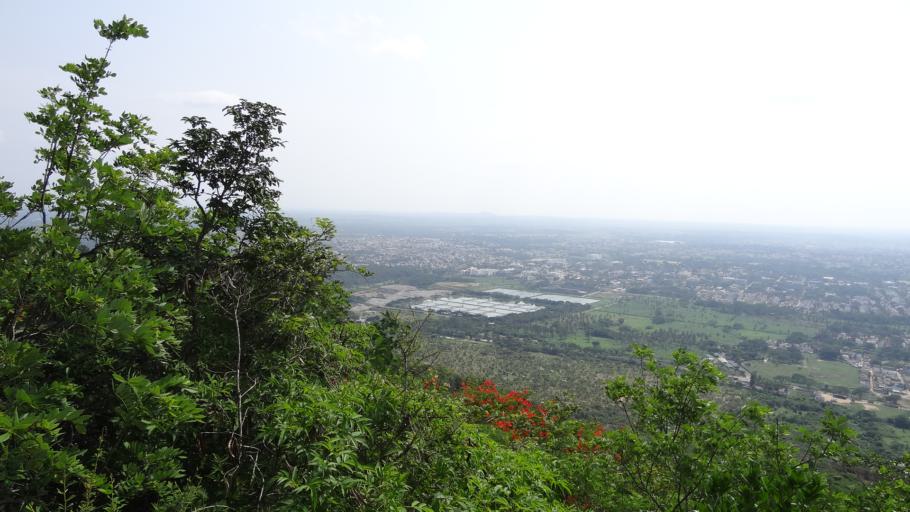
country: IN
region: Karnataka
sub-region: Mysore
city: Mysore
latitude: 12.2775
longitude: 76.6685
